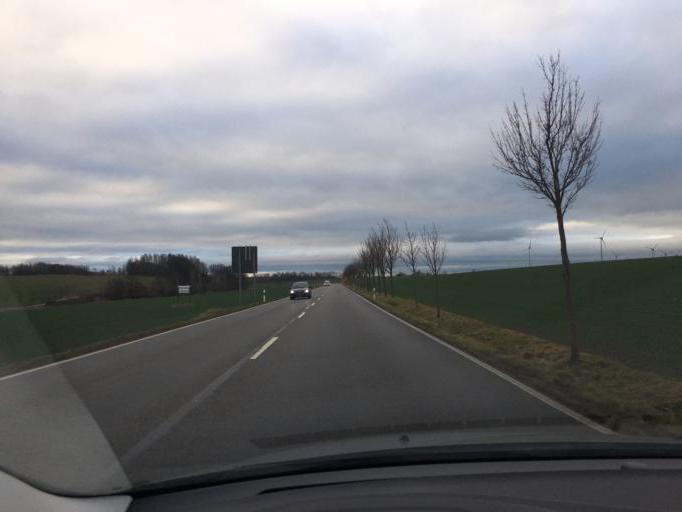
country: DE
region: Thuringia
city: Juckelberg
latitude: 50.9611
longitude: 12.6596
